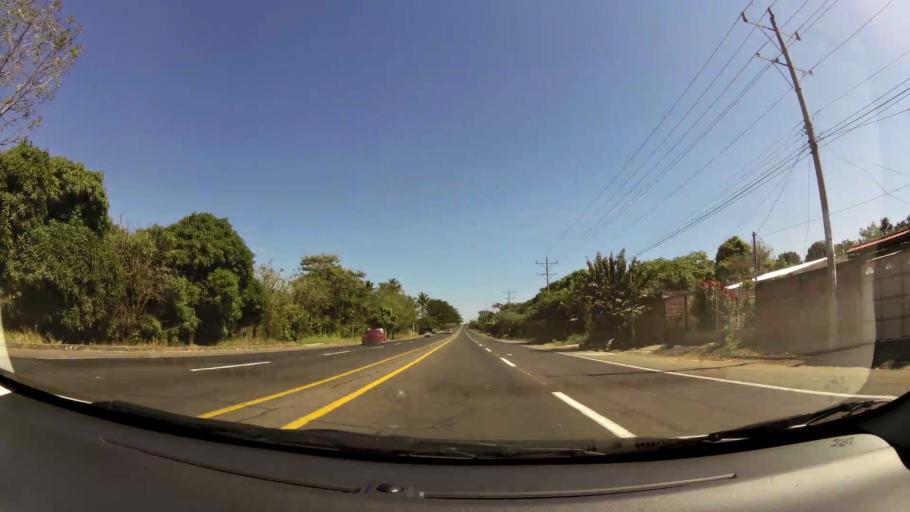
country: SV
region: Ahuachapan
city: Atiquizaya
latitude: 13.9724
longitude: -89.7184
